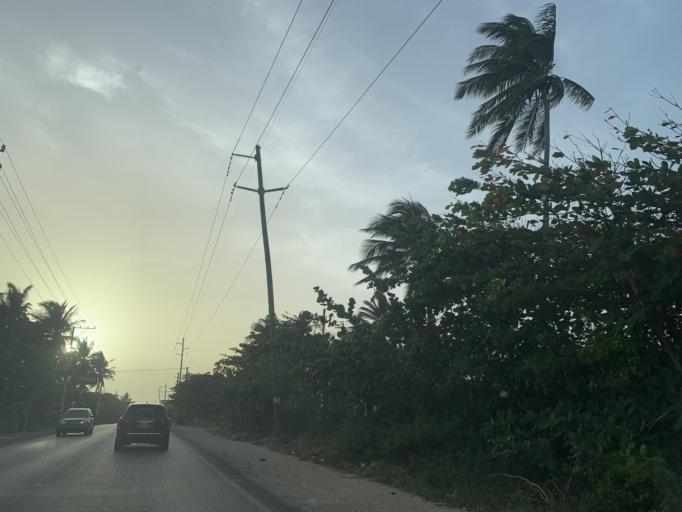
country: DO
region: Puerto Plata
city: Cabarete
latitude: 19.7659
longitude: -70.4284
